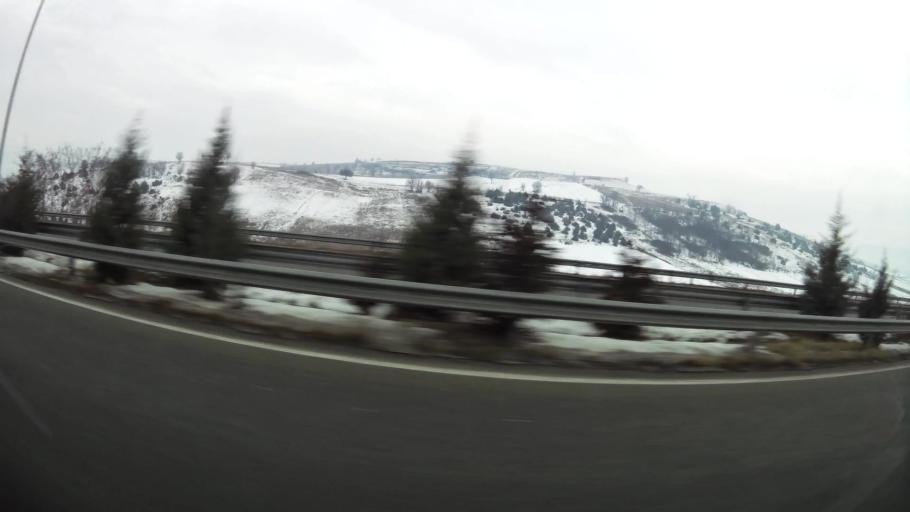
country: MK
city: Kondovo
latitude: 42.0198
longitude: 21.3312
